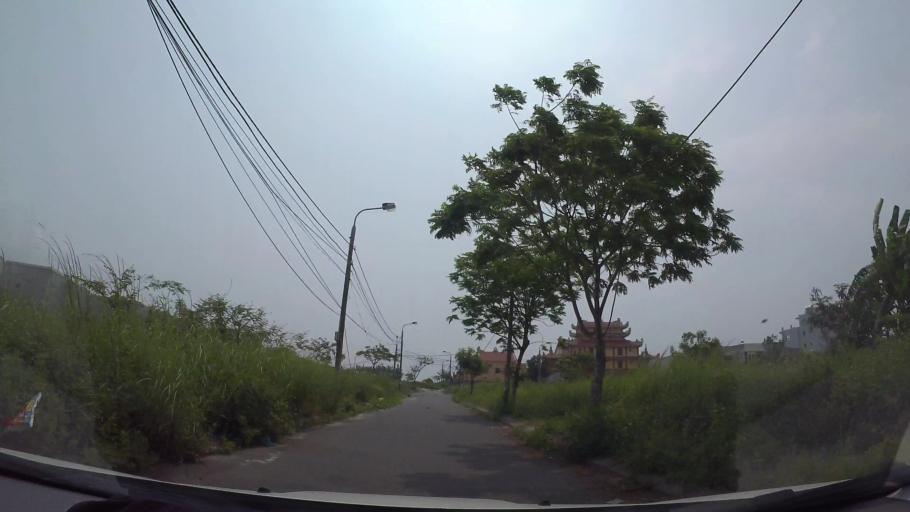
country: VN
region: Da Nang
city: Son Tra
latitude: 16.1028
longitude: 108.2552
